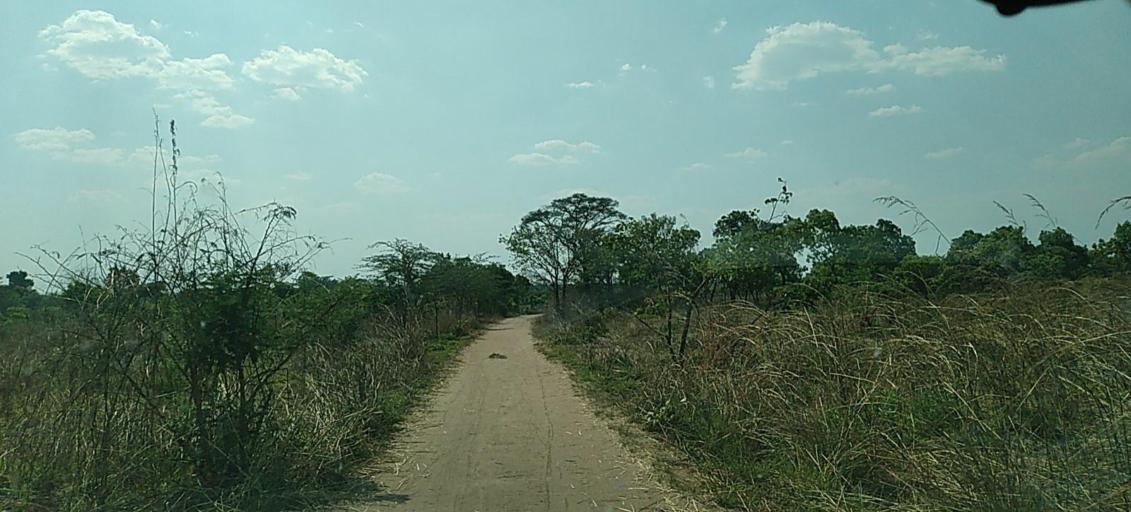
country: ZM
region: North-Western
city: Kalengwa
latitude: -13.1159
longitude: 24.9954
